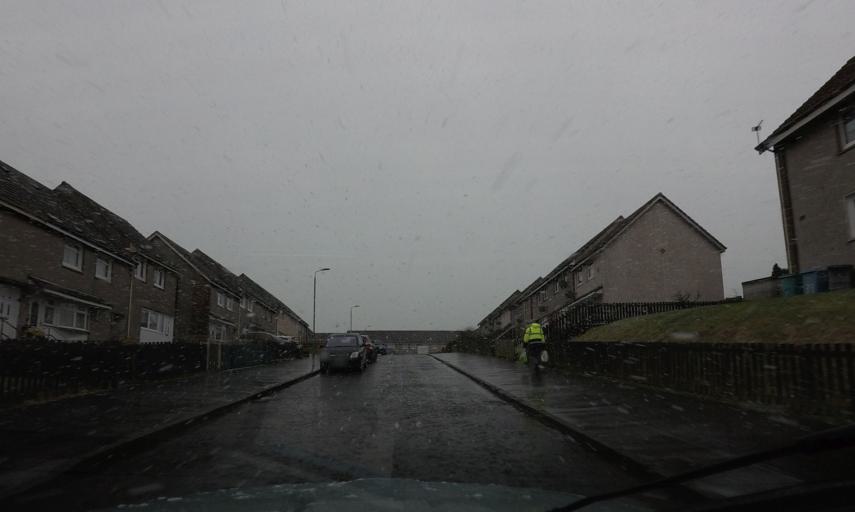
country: GB
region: Scotland
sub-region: North Lanarkshire
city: Caldercruix
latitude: 55.8426
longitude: -3.8718
